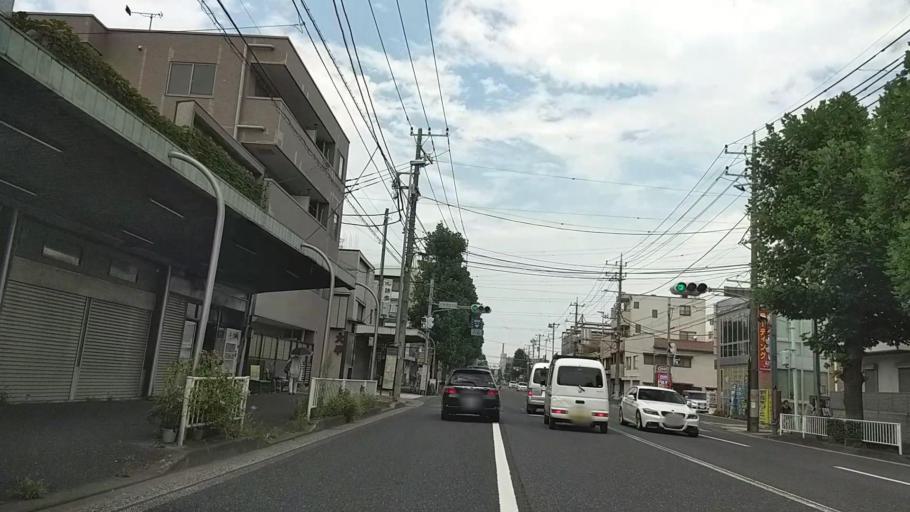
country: JP
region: Kanagawa
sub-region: Kawasaki-shi
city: Kawasaki
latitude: 35.5267
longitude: 139.6696
